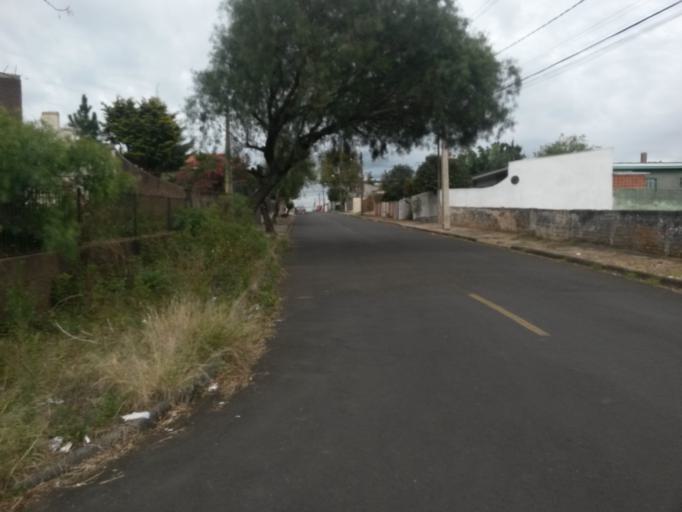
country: BR
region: Parana
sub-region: Guarapuava
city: Guarapuava
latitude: -25.3869
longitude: -51.4578
